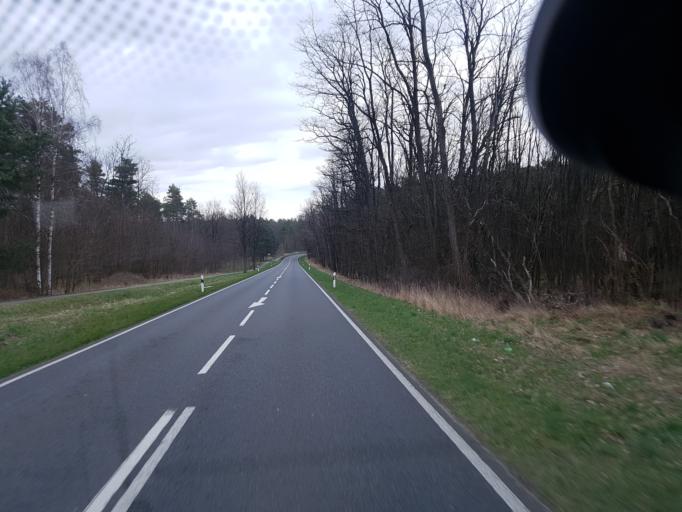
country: DE
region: Brandenburg
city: Eisenhuettenstadt
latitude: 52.1507
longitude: 14.5792
